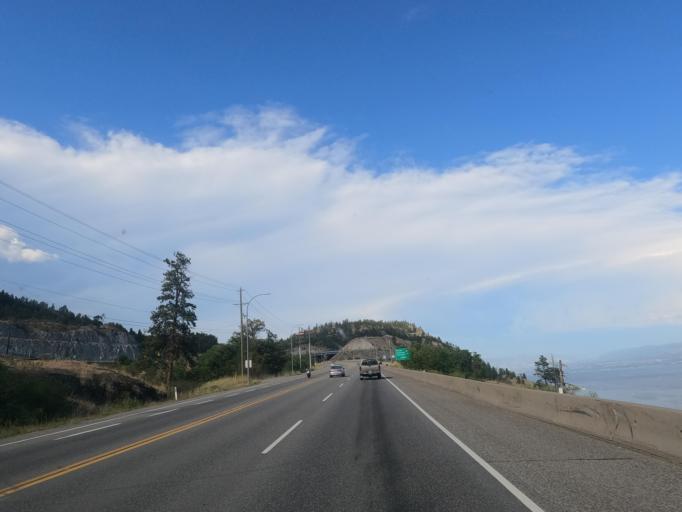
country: CA
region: British Columbia
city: Peachland
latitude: 49.8019
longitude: -119.6695
